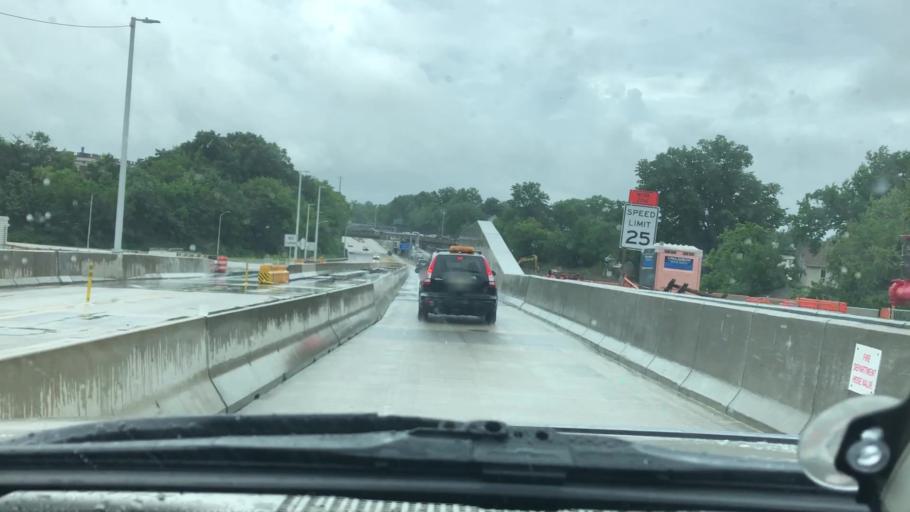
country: US
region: New York
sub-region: Richmond County
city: Bloomfield
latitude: 40.6333
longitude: -74.1454
